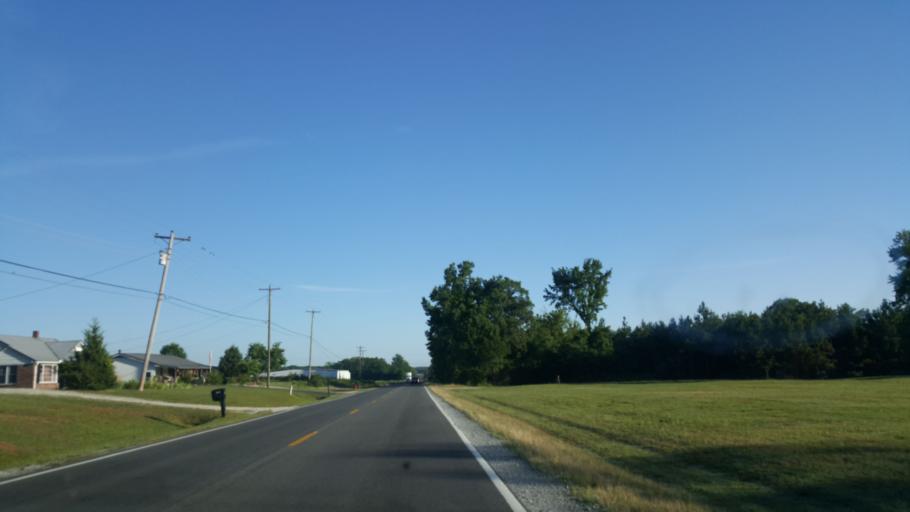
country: US
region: Tennessee
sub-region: Henderson County
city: Lexington
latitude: 35.6056
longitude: -88.3944
